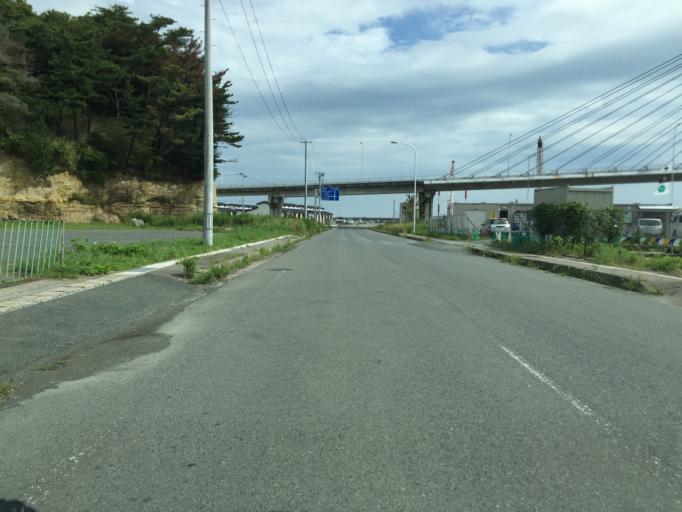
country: JP
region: Miyagi
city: Marumori
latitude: 37.8253
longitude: 140.9733
